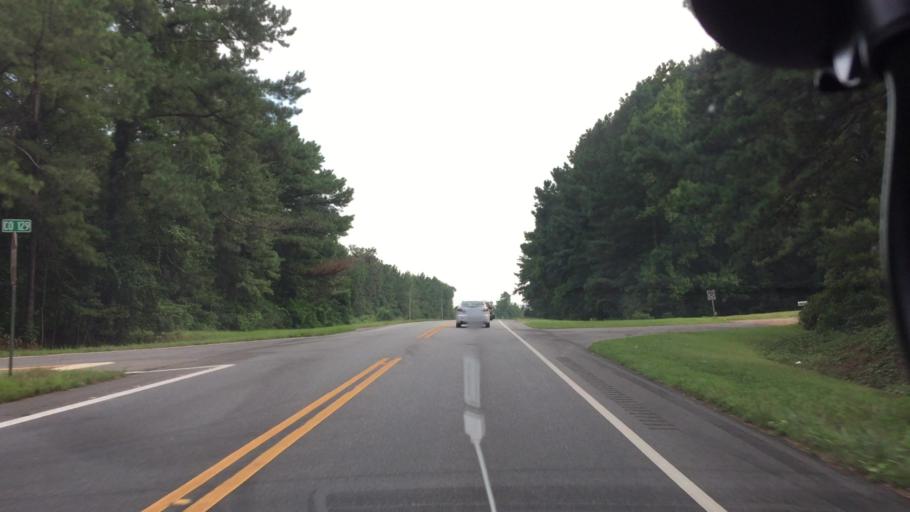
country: US
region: Alabama
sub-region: Coffee County
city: New Brockton
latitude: 31.5495
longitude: -85.9197
